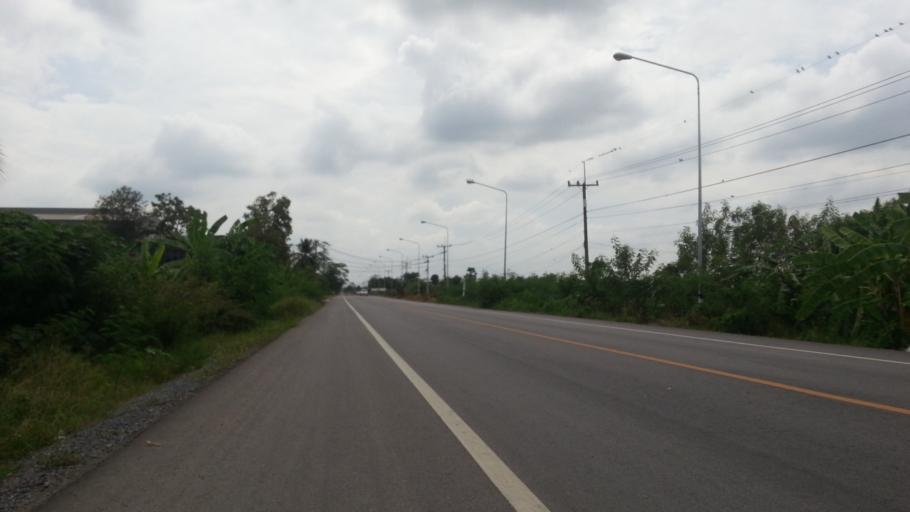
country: TH
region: Pathum Thani
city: Ban Rangsit
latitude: 14.0369
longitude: 100.8440
